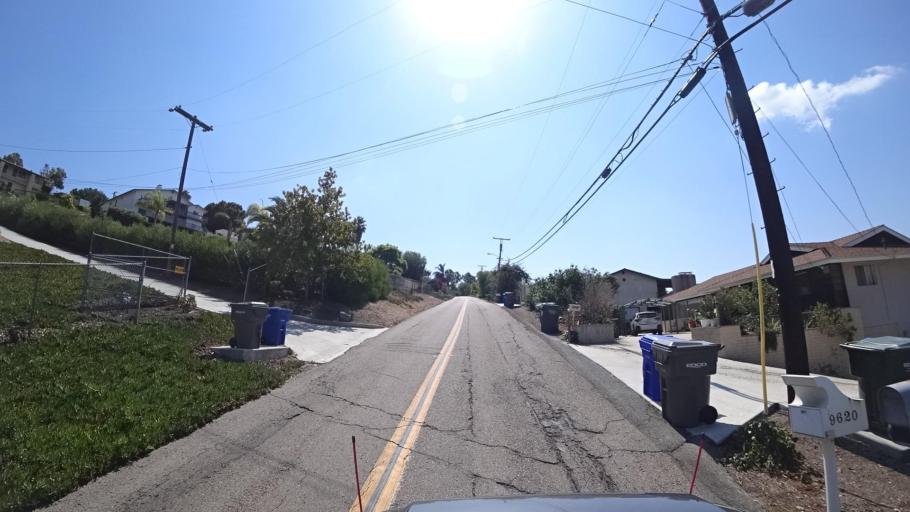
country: US
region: California
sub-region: San Diego County
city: Spring Valley
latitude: 32.7356
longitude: -116.9913
